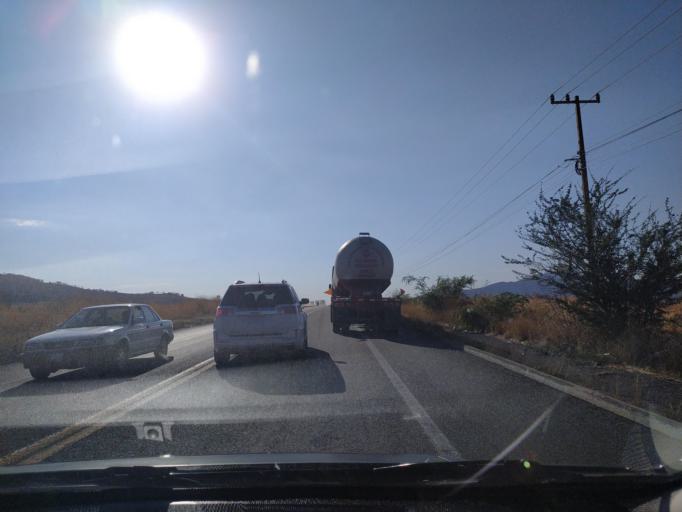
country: MX
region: Michoacan
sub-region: Yurecuaro
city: Yurecuaro
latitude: 20.3394
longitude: -102.1978
